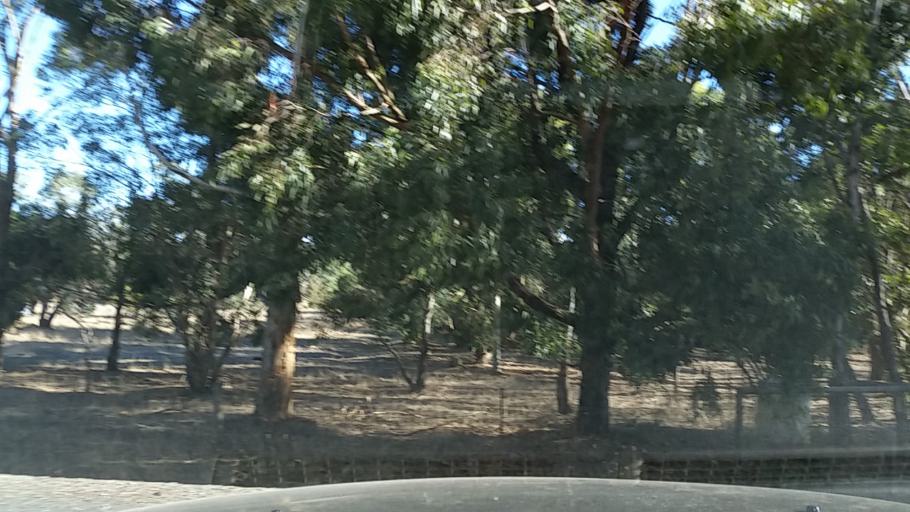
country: AU
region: South Australia
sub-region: Mount Barker
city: Nairne
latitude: -35.0392
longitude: 138.9242
